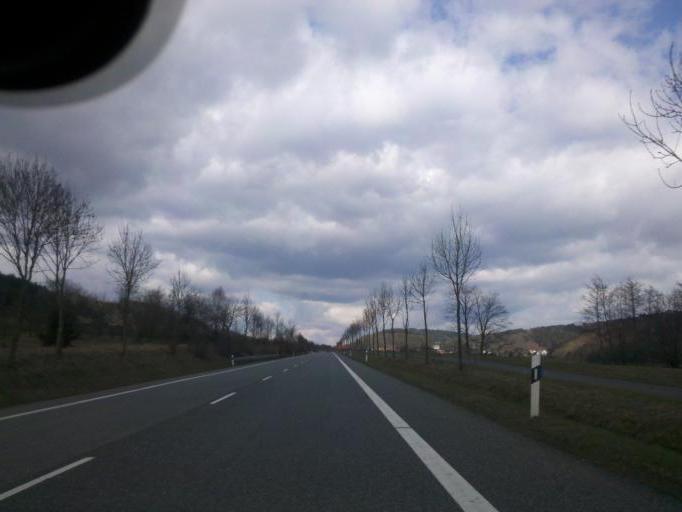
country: DE
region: Hesse
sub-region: Regierungsbezirk Giessen
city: Siegbach
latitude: 50.8143
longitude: 8.3627
